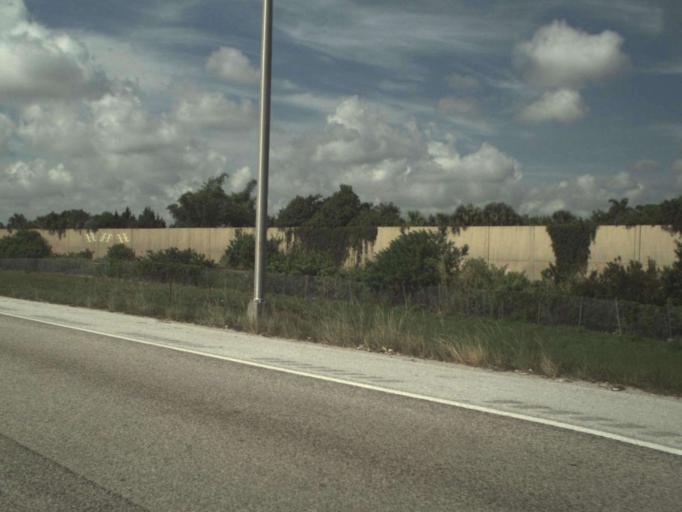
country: US
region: Florida
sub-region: Palm Beach County
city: Lake Clarke Shores
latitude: 26.6627
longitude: -80.0711
